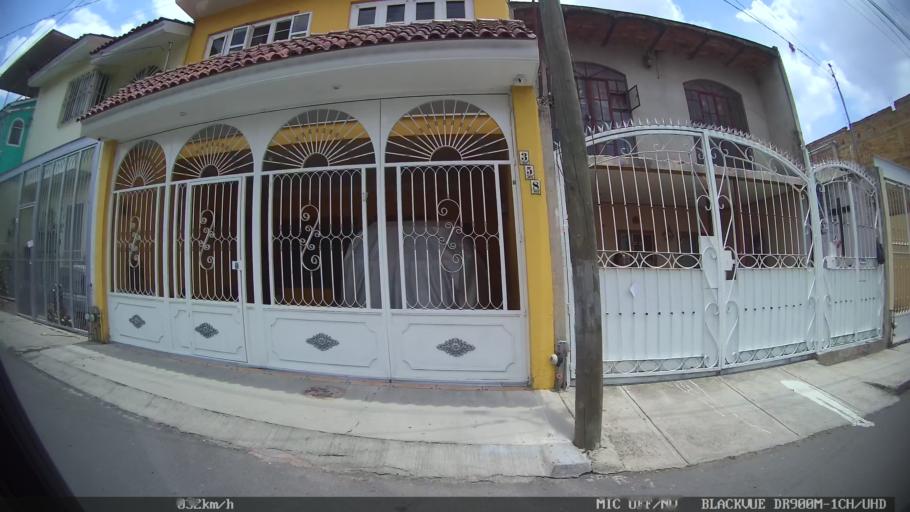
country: MX
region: Jalisco
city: Tonala
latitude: 20.6559
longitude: -103.2264
